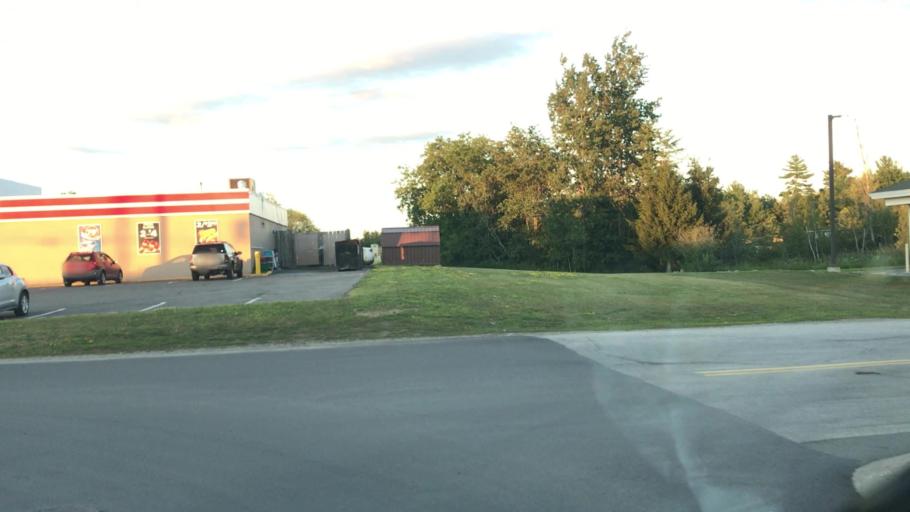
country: US
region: Maine
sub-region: Penobscot County
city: Lincoln
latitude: 45.3618
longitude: -68.5160
